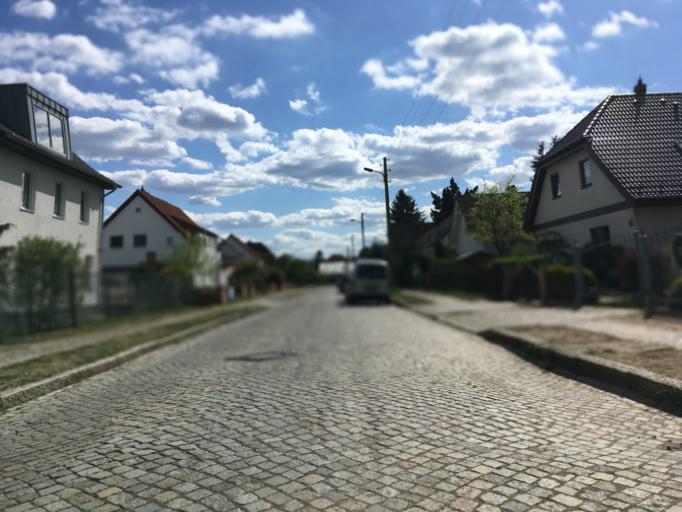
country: DE
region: Berlin
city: Hellersdorf
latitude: 52.5261
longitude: 13.6306
